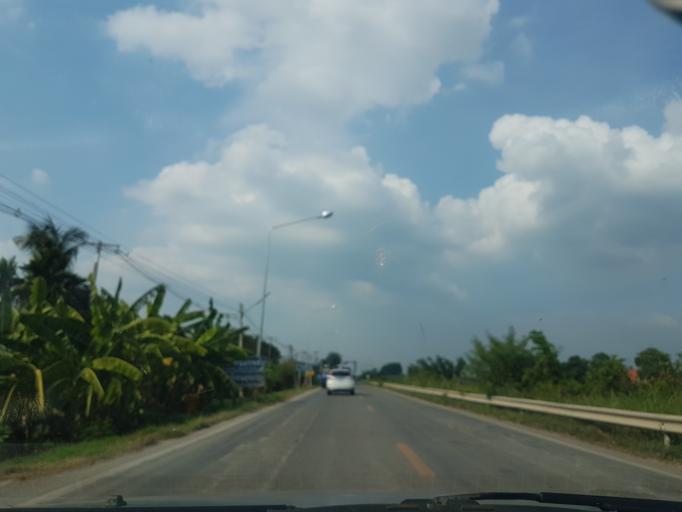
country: TH
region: Phra Nakhon Si Ayutthaya
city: Phachi
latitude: 14.4160
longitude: 100.7825
